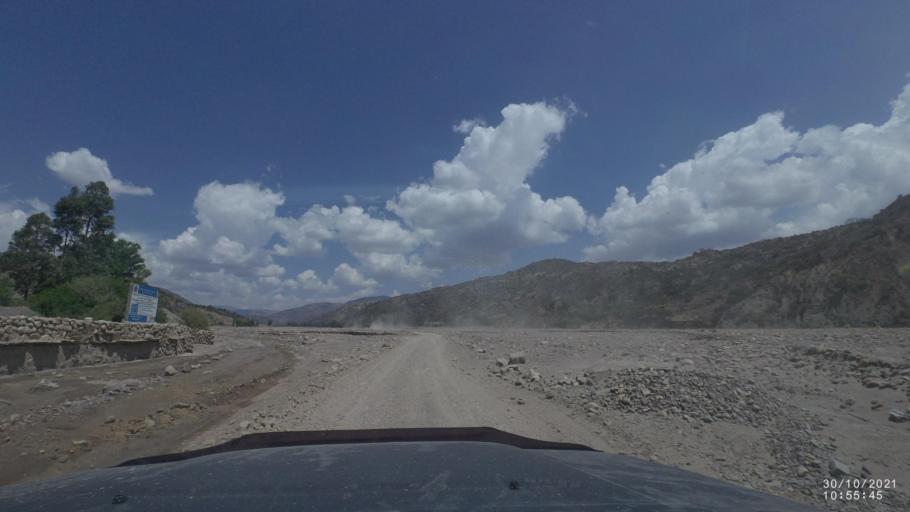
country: BO
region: Cochabamba
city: Sipe Sipe
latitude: -17.5412
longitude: -66.4910
